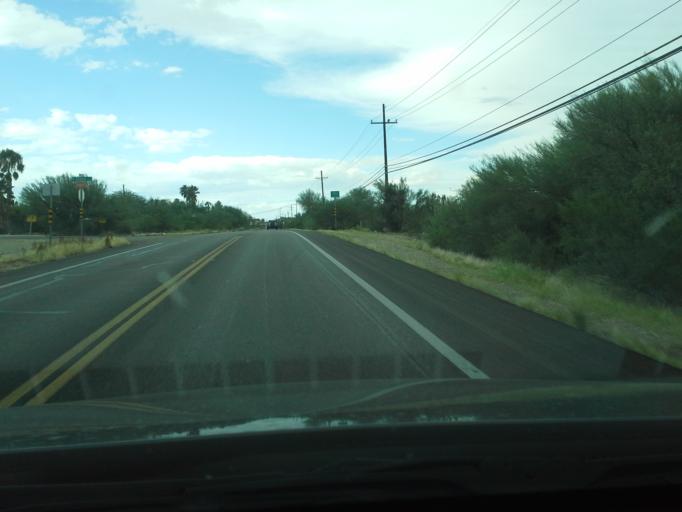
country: US
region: Arizona
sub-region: Pima County
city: South Tucson
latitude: 32.2166
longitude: -111.0203
